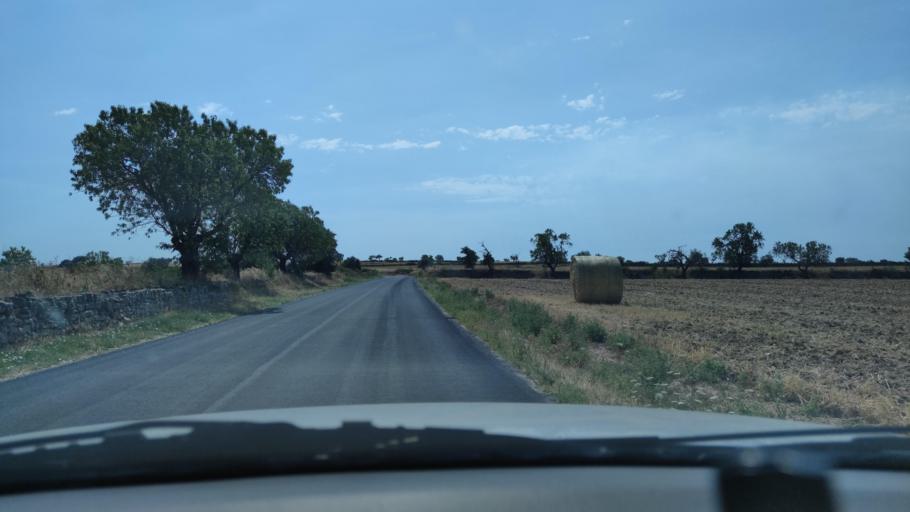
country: ES
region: Catalonia
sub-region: Provincia de Lleida
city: Ivorra
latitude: 41.7785
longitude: 1.3139
